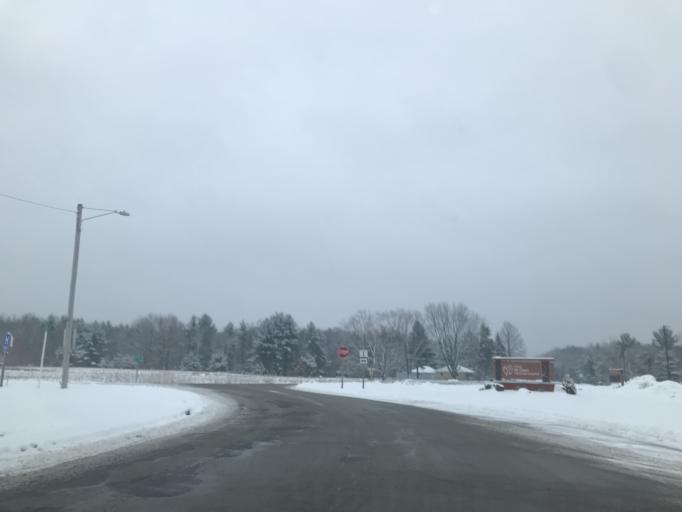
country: US
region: Wisconsin
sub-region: Oconto County
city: Oconto Falls
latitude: 44.8656
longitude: -88.1266
